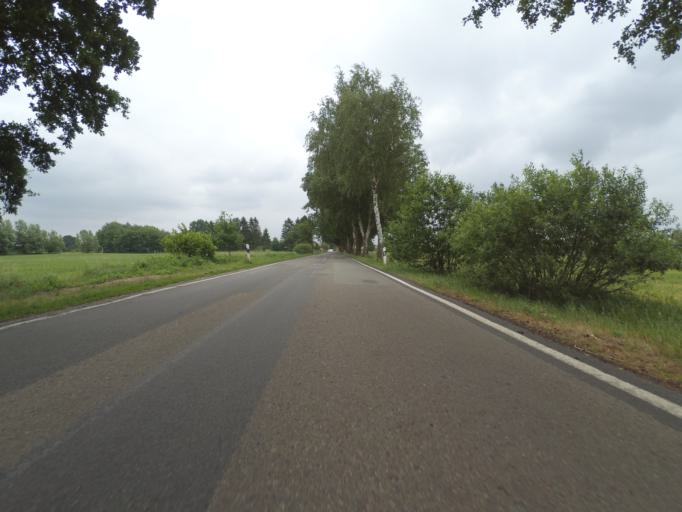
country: DE
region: Mecklenburg-Vorpommern
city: Siggelkow
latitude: 53.3814
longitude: 11.9725
